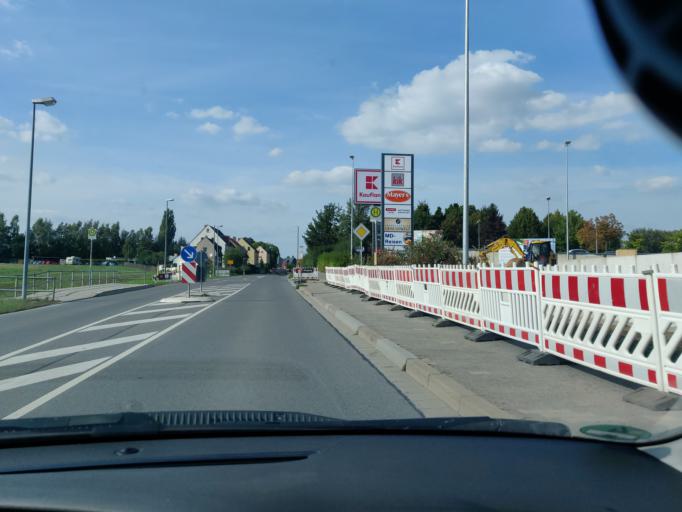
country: DE
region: Saxony
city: Mittweida
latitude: 50.9941
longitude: 12.9643
